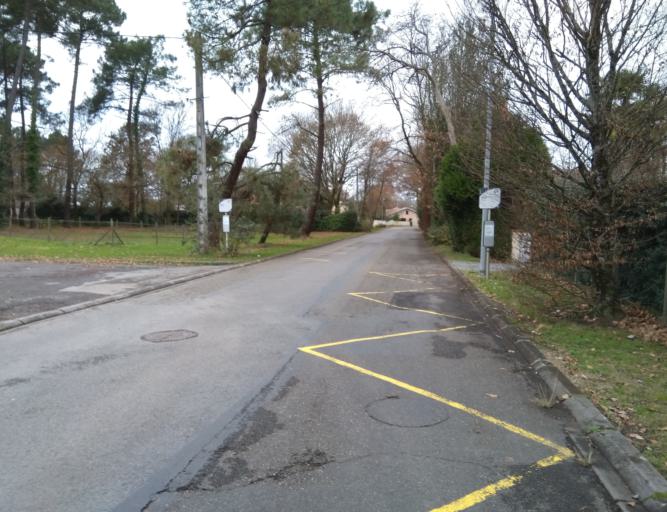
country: FR
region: Aquitaine
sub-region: Departement des Landes
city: Oeyreluy
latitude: 43.6894
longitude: -1.0737
